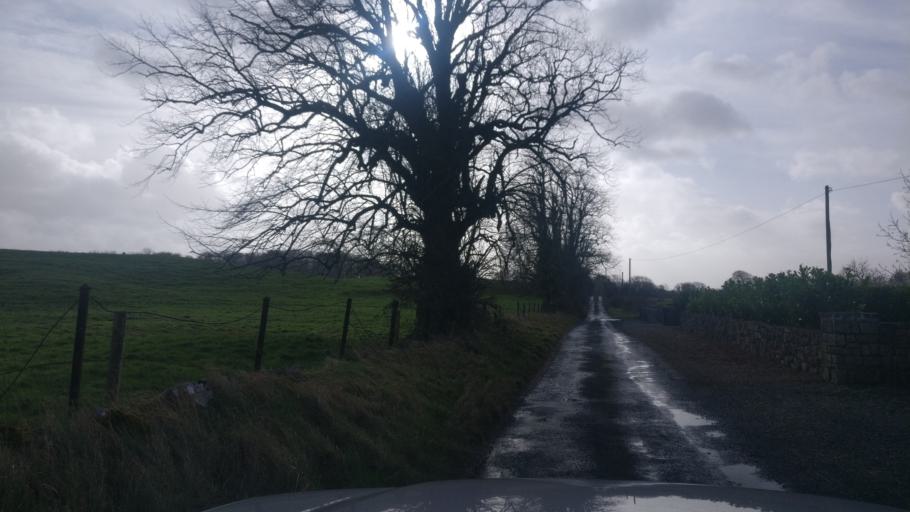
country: IE
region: Connaught
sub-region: County Galway
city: Loughrea
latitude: 53.2752
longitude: -8.5942
